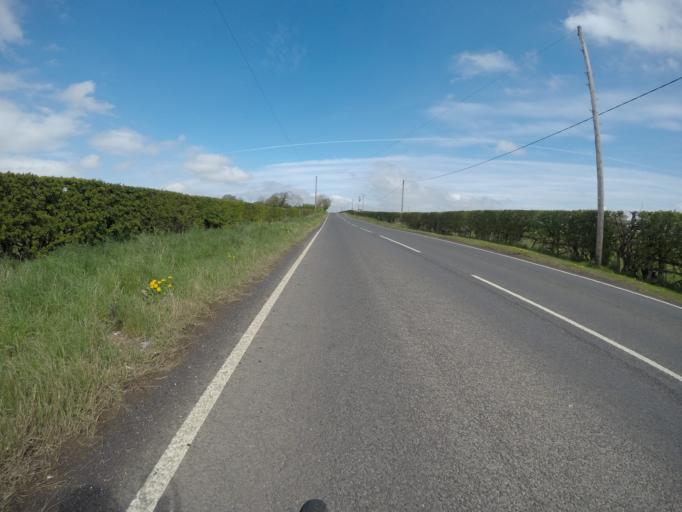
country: GB
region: Scotland
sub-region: East Ayrshire
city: Kilmaurs
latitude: 55.6607
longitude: -4.5497
